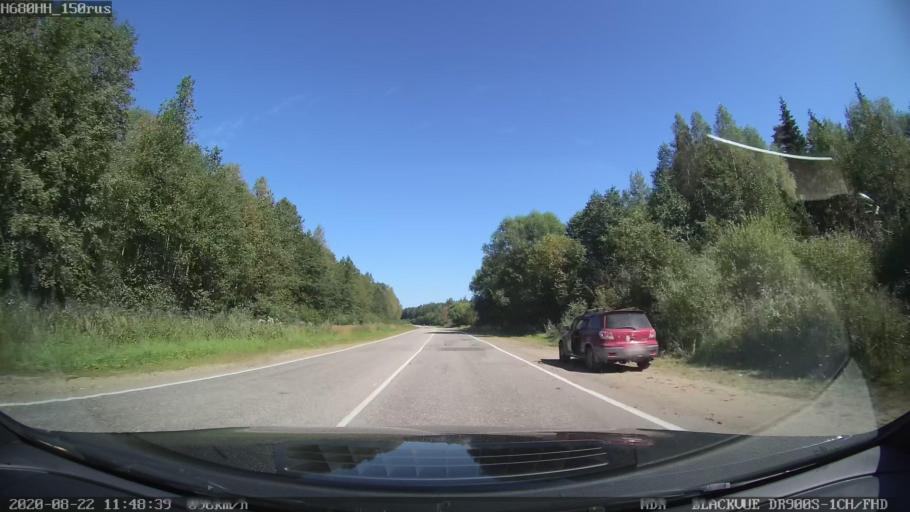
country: RU
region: Tverskaya
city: Sakharovo
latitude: 57.0656
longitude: 36.1064
